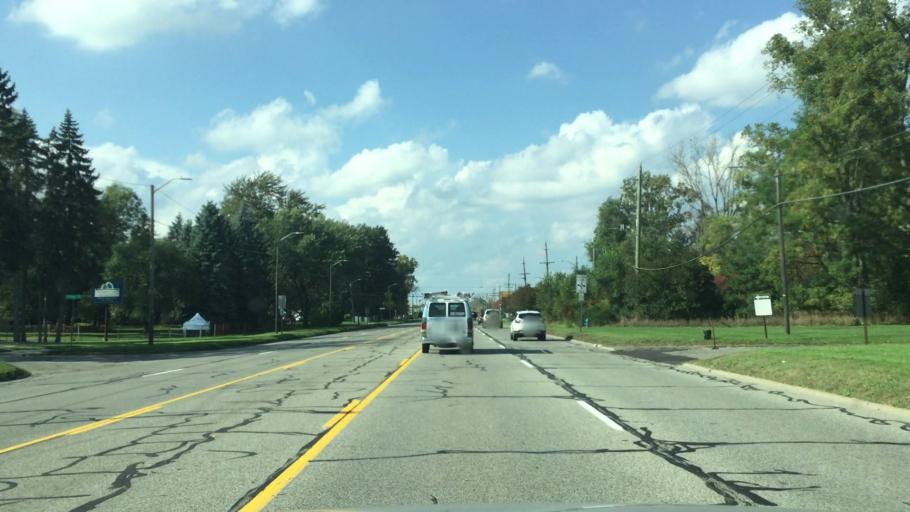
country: US
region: Michigan
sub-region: Oakland County
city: Keego Harbor
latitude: 42.6483
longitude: -83.3652
